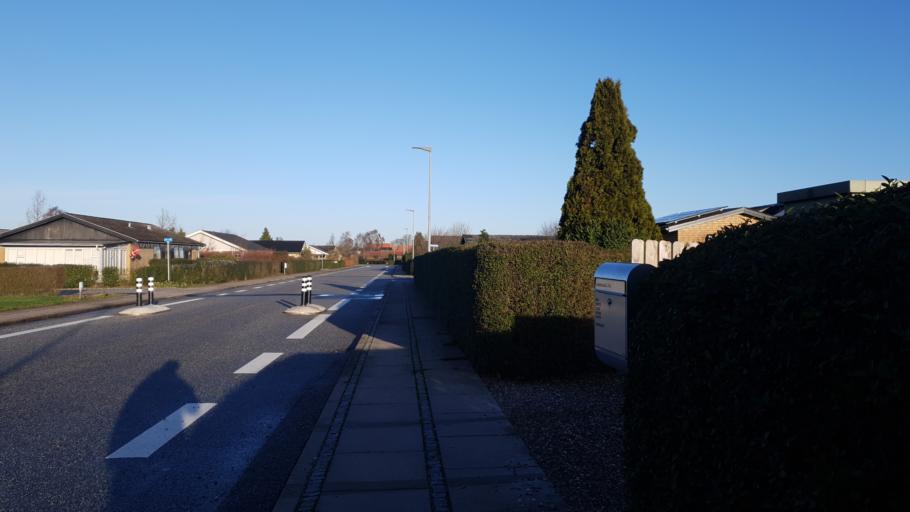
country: DK
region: Central Jutland
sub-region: Hedensted Kommune
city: Hedensted
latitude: 55.8006
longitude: 9.6917
